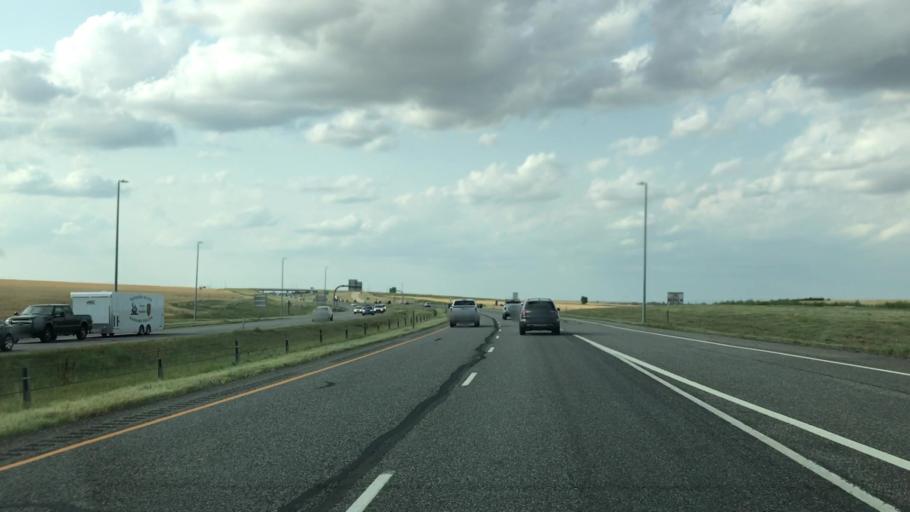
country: US
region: Colorado
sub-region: Adams County
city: Aurora
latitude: 39.8033
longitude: -104.7161
